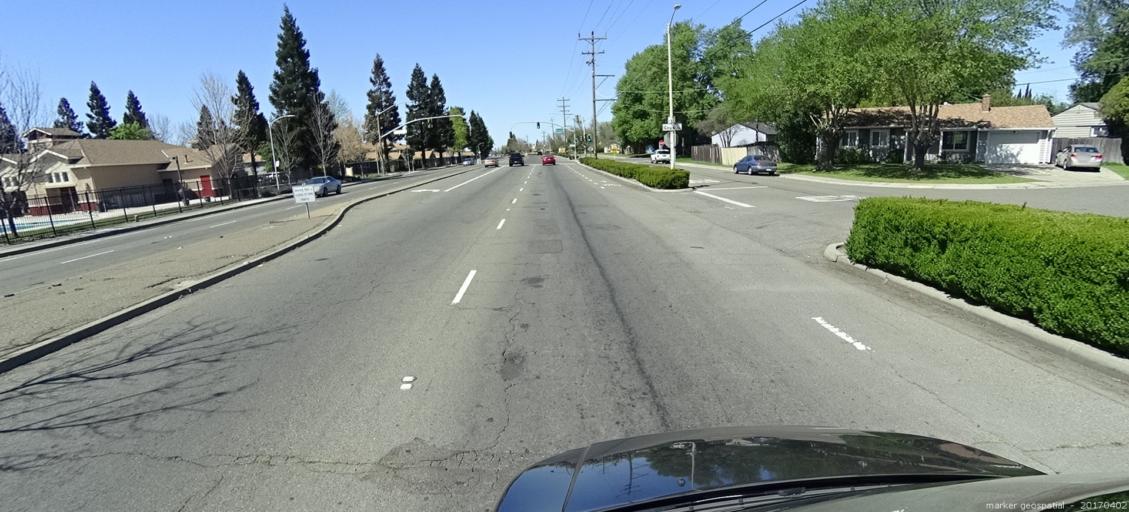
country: US
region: California
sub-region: Sacramento County
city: Parkway
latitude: 38.4866
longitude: -121.4546
